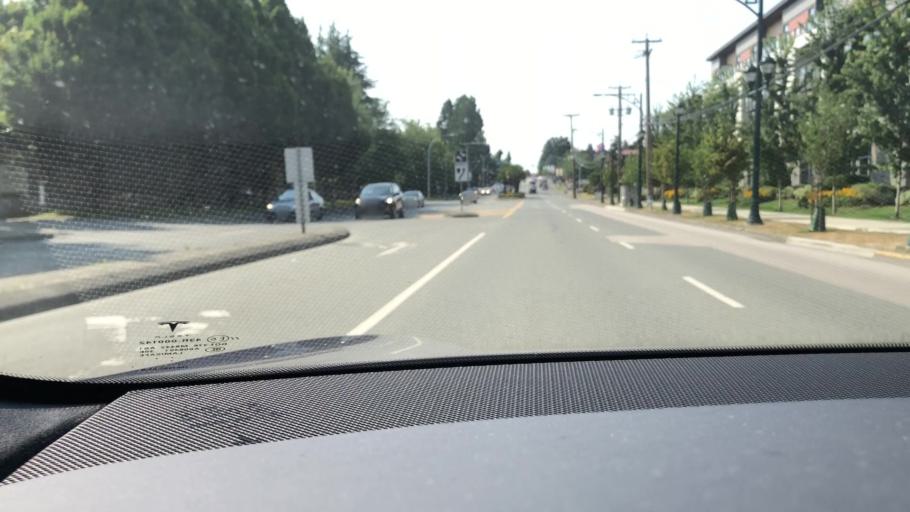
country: US
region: Washington
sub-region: Whatcom County
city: Point Roberts
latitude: 49.0347
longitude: -123.0687
